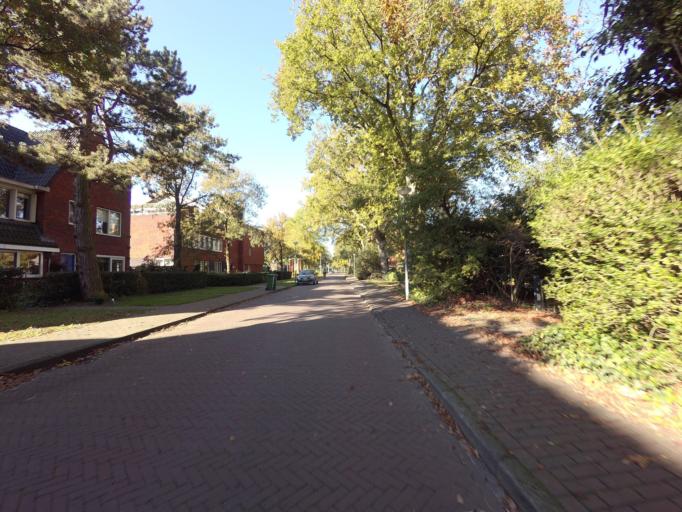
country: NL
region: North Holland
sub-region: Gemeente Laren
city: Laren
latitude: 52.2467
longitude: 5.2365
